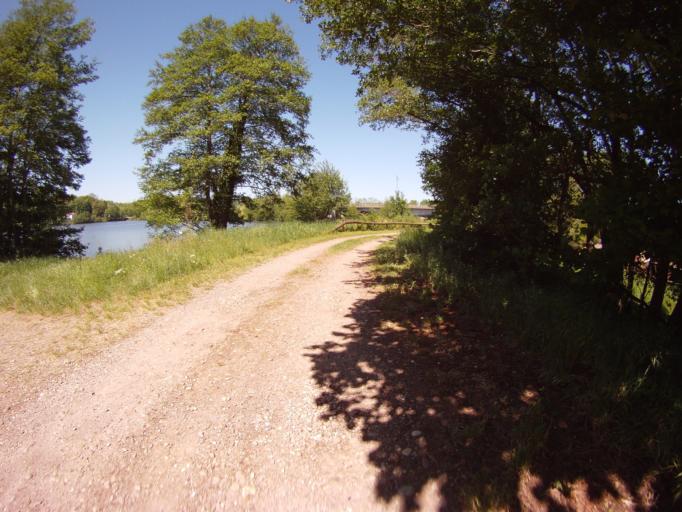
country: FR
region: Lorraine
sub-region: Departement de Meurthe-et-Moselle
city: Dommartin-les-Toul
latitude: 48.6550
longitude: 5.9001
